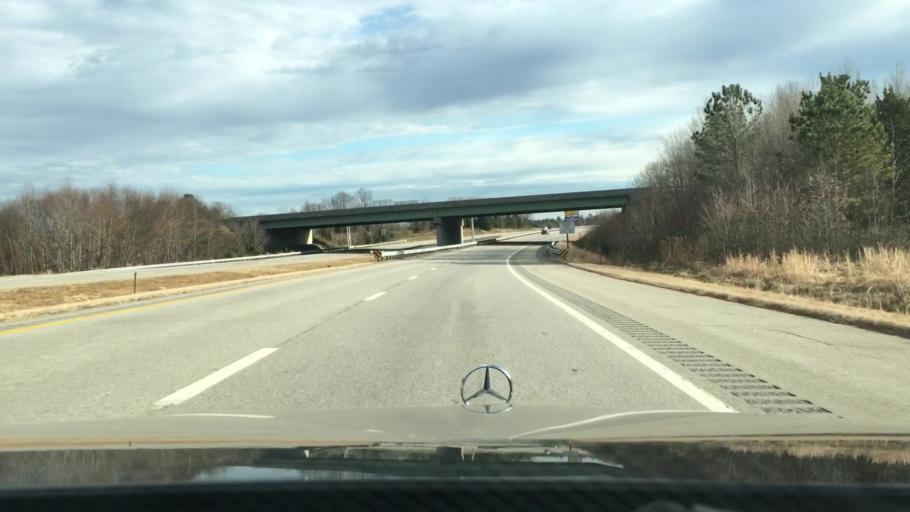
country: US
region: Virginia
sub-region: Pittsylvania County
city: Mount Hermon
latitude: 36.6995
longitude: -79.3651
